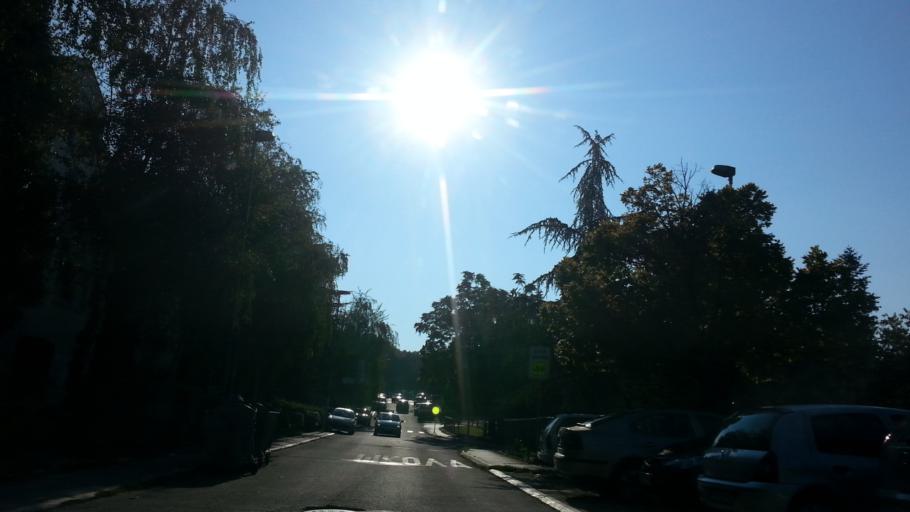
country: RS
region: Central Serbia
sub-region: Belgrade
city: Cukarica
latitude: 44.7664
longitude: 20.4179
